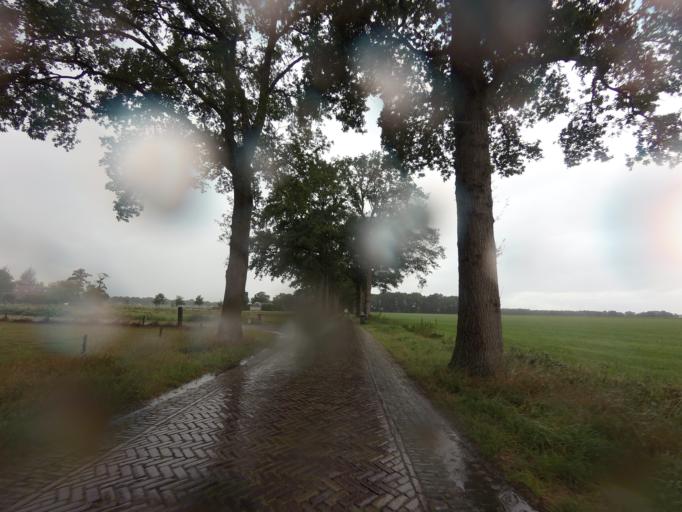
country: NL
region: Drenthe
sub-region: Gemeente Hoogeveen
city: Hoogeveen
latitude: 52.6362
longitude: 6.4661
